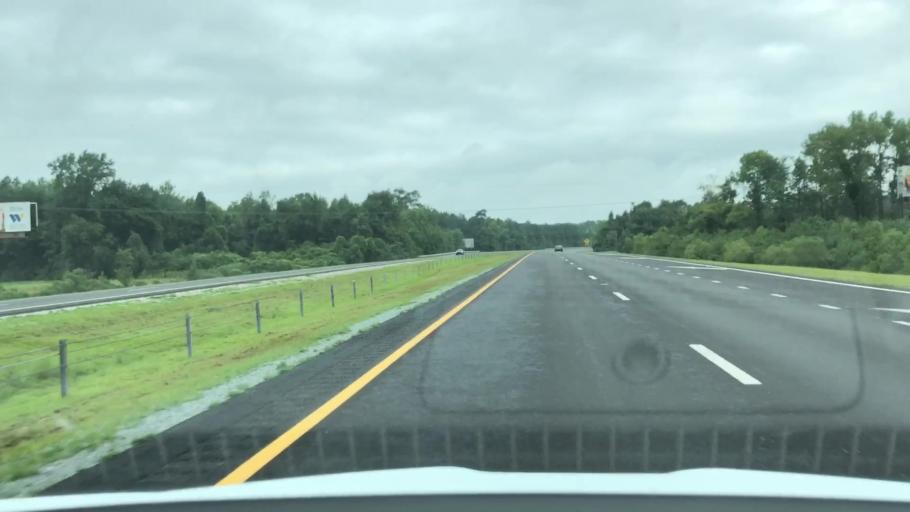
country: US
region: North Carolina
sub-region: Wayne County
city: Fremont
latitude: 35.4994
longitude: -77.9982
